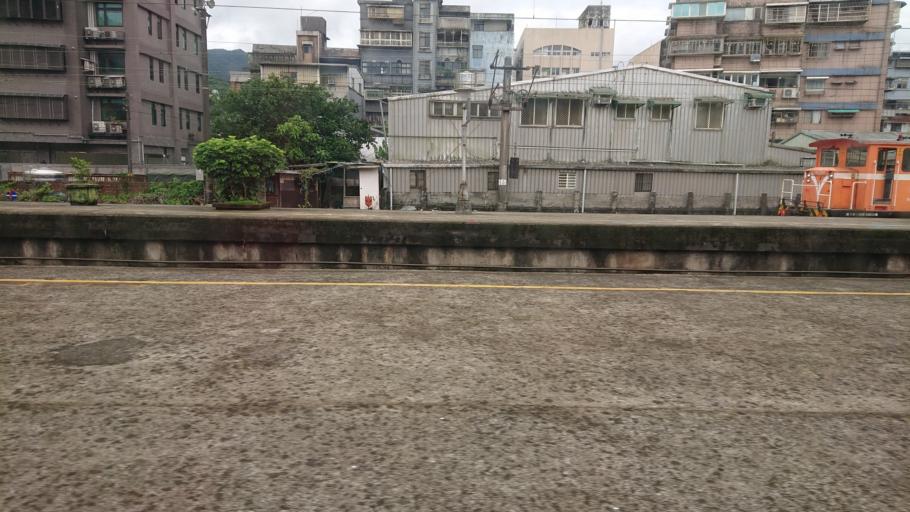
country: TW
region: Taiwan
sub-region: Keelung
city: Keelung
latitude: 25.1087
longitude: 121.8078
